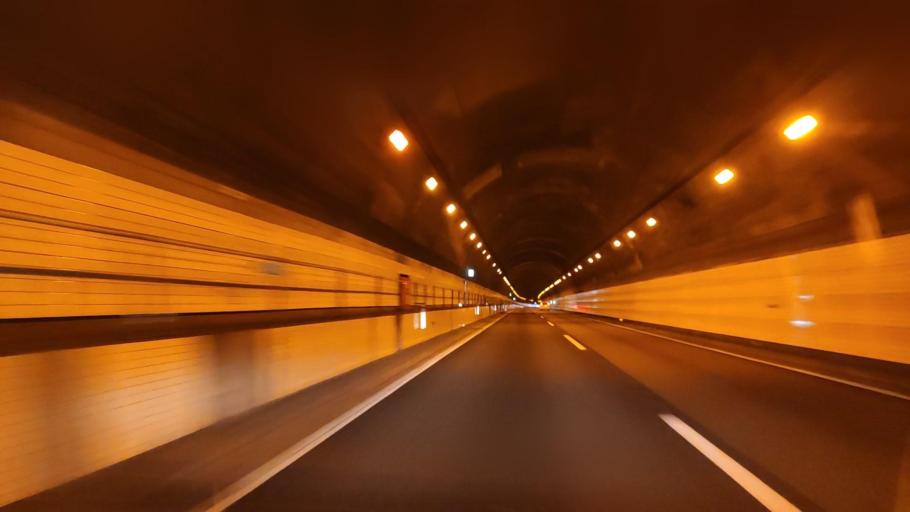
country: JP
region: Iwate
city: Ichinoseki
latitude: 38.9911
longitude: 141.0983
